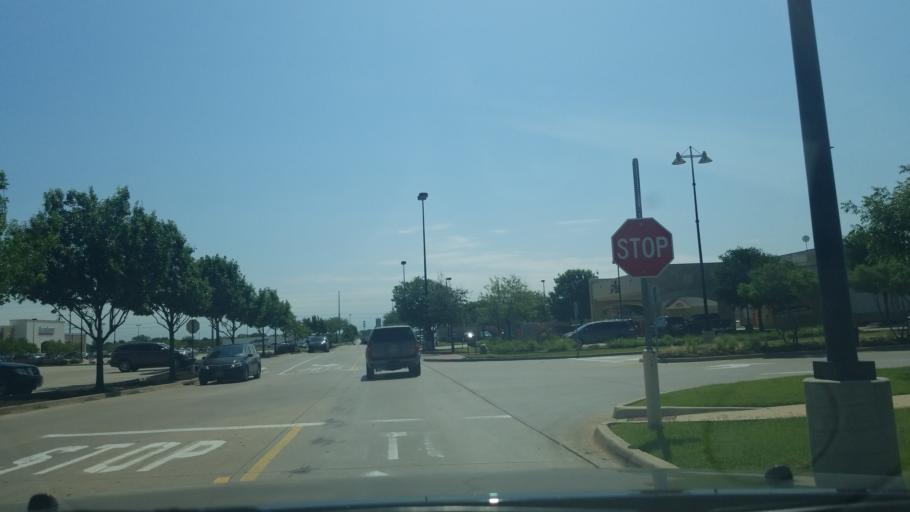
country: US
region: Texas
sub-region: Denton County
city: Denton
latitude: 33.2308
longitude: -97.1649
